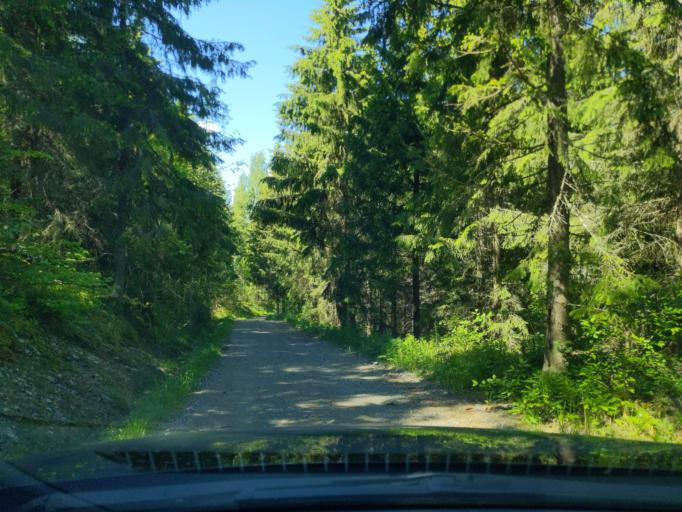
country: FI
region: Paijanne Tavastia
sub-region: Lahti
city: Lahti
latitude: 61.0540
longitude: 25.6948
